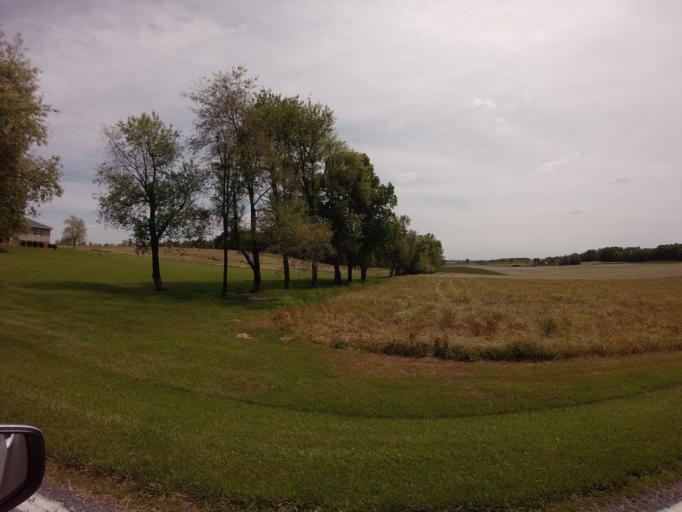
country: US
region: Maryland
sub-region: Frederick County
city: Linganore
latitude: 39.5150
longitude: -77.2267
